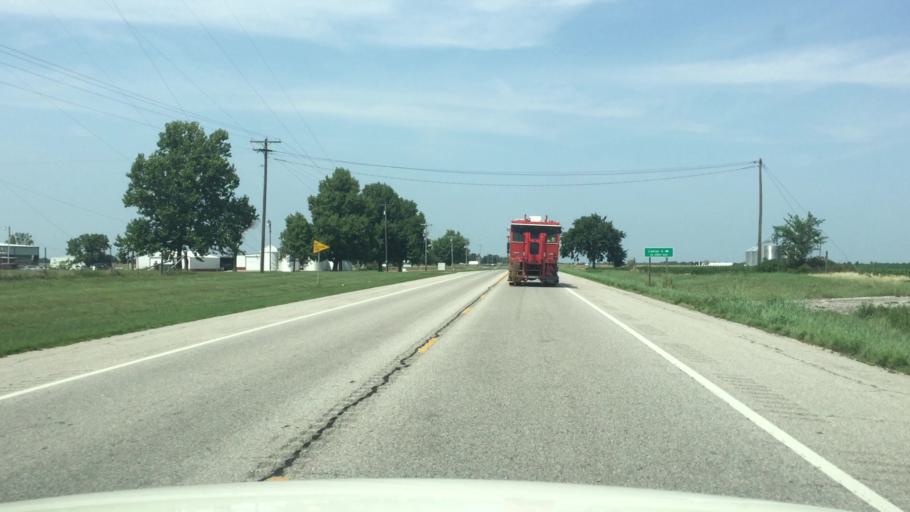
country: US
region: Missouri
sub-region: Jasper County
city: Carl Junction
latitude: 37.2197
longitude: -94.7049
